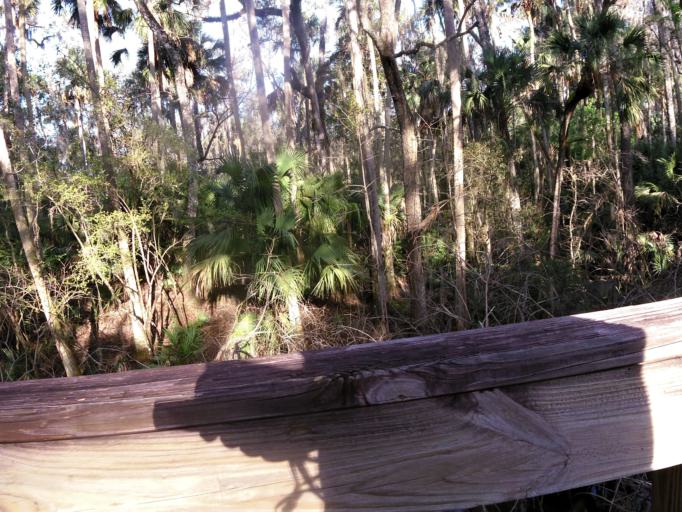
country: US
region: Florida
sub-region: Volusia County
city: Orange City
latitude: 28.9458
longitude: -81.3390
